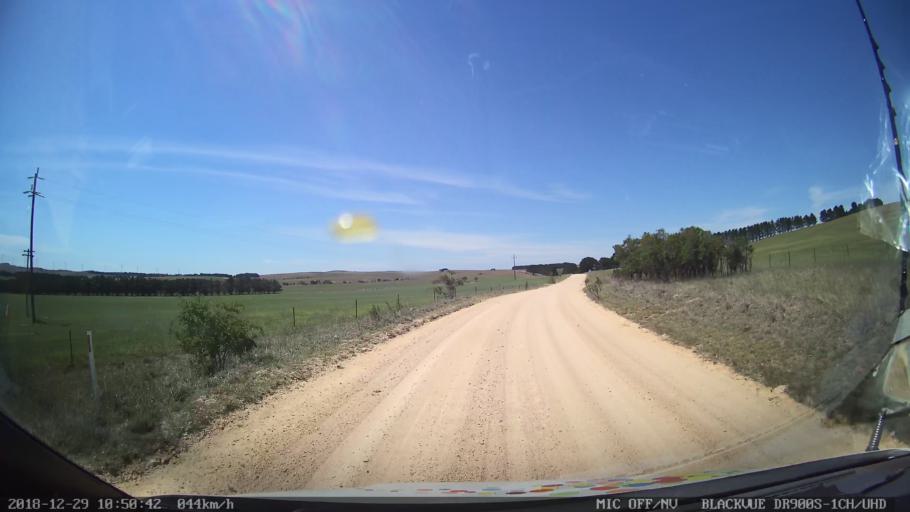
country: AU
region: New South Wales
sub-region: Palerang
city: Bungendore
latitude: -35.0835
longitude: 149.5241
